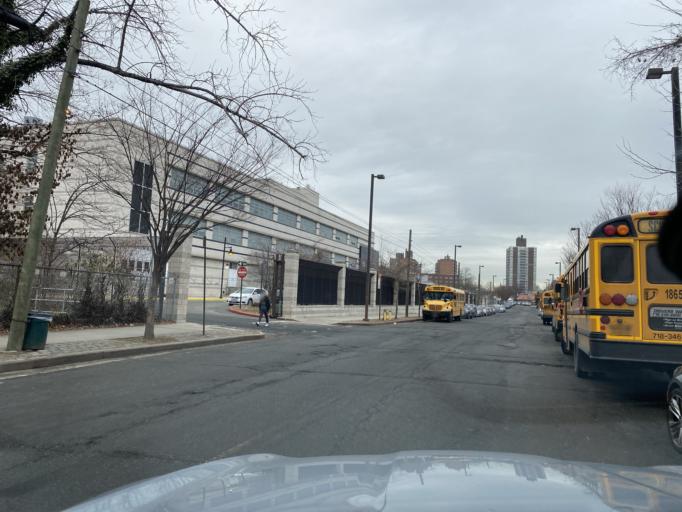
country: US
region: New York
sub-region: New York County
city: Inwood
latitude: 40.8780
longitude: -73.9117
